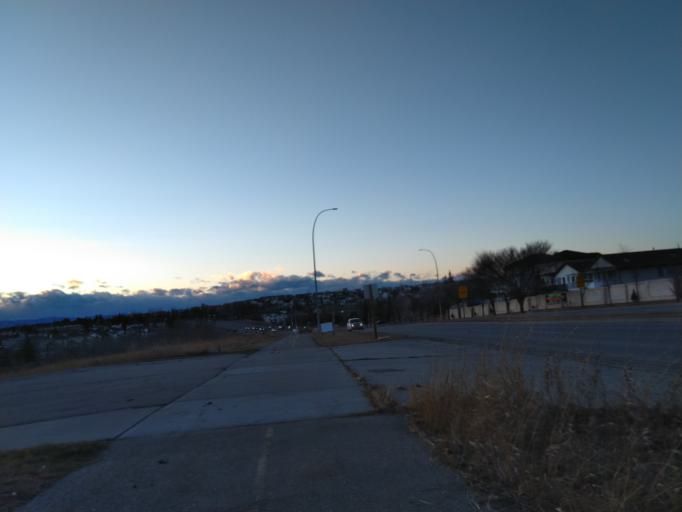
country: CA
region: Alberta
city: Calgary
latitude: 51.1252
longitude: -114.2360
